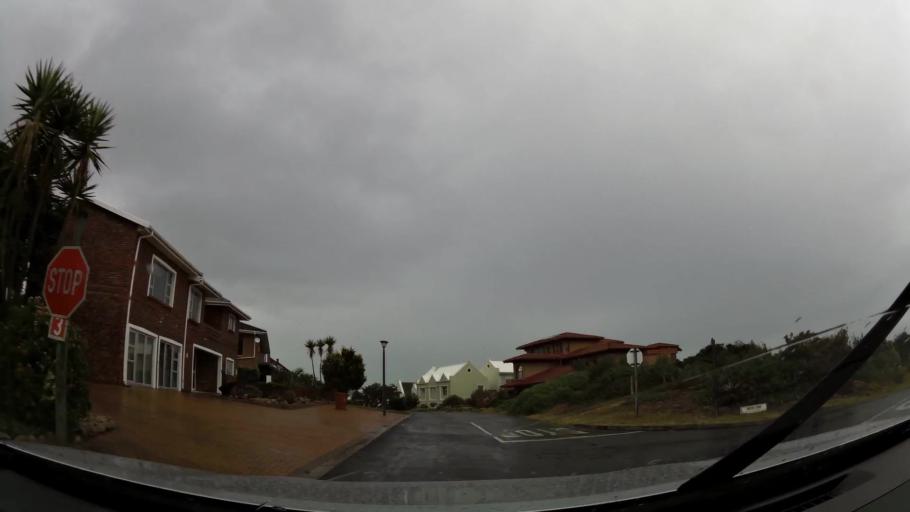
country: ZA
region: Western Cape
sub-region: Eden District Municipality
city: Mossel Bay
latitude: -34.0533
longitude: 22.2479
